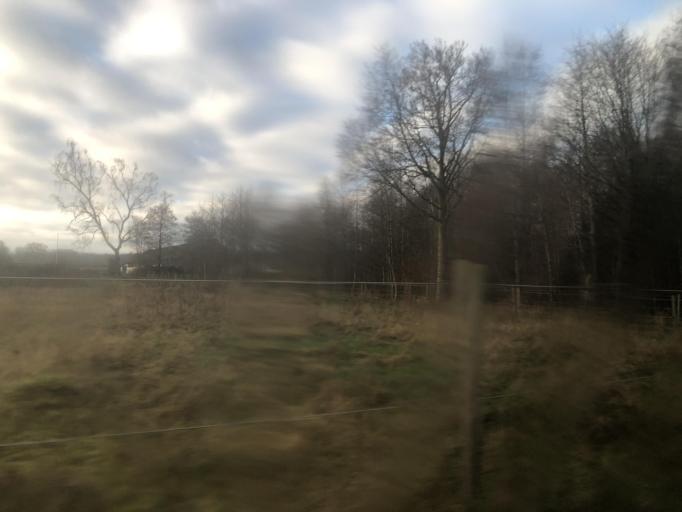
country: SE
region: Skane
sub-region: Lunds Kommun
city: Veberod
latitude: 55.6050
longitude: 13.5369
